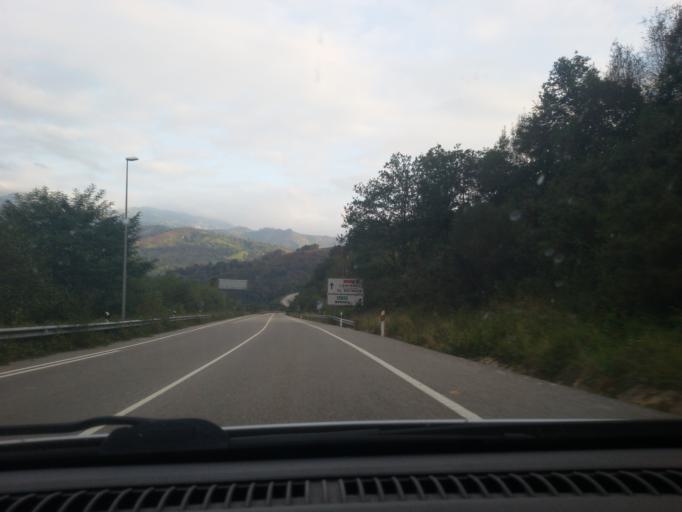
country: ES
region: Asturias
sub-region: Province of Asturias
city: Bimenes
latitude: 43.3472
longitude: -5.5861
